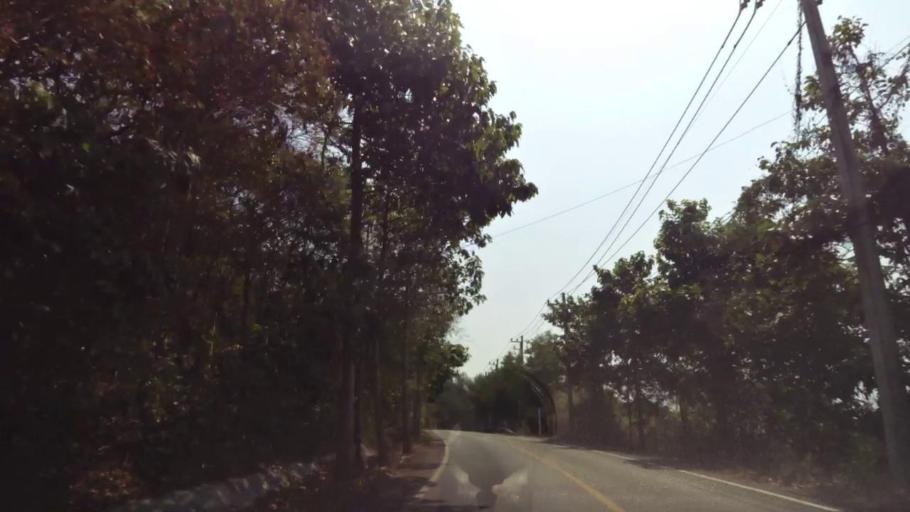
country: TH
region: Chanthaburi
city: Tha Mai
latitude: 12.5307
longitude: 101.9456
